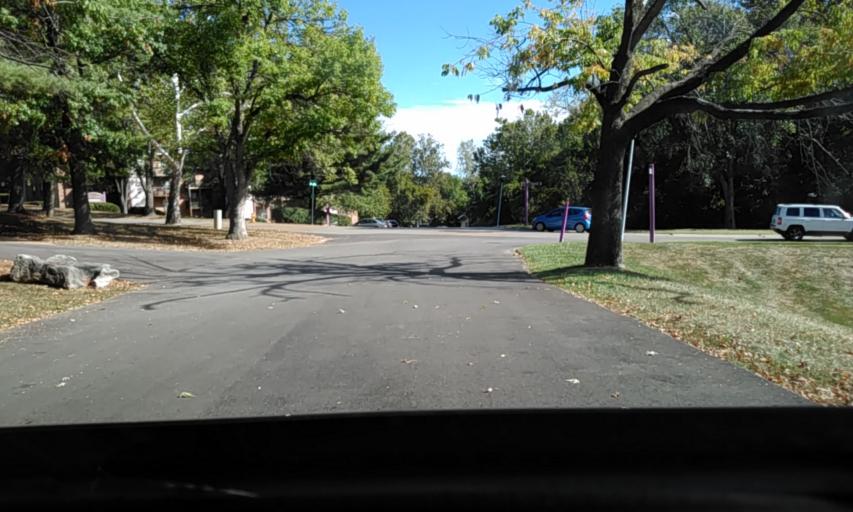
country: US
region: Missouri
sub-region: Saint Louis County
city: Mehlville
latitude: 38.4881
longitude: -90.3509
